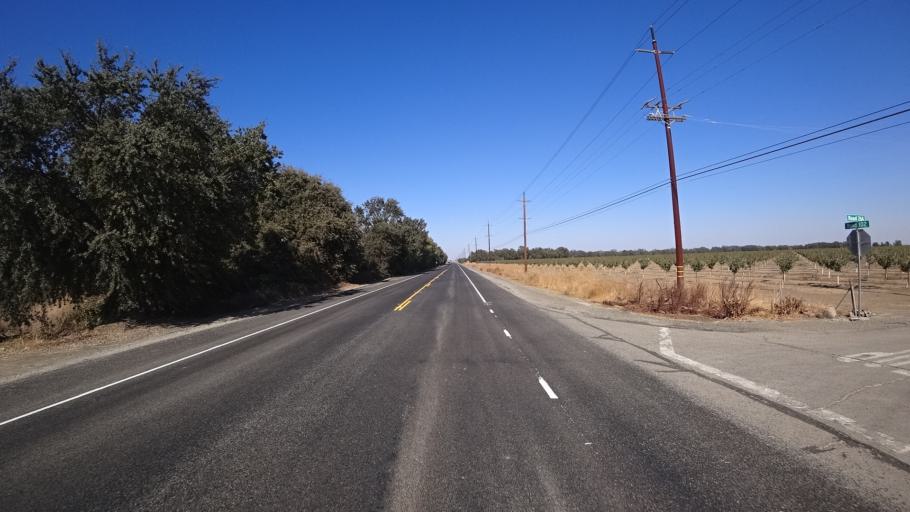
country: US
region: California
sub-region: Yolo County
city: Woodland
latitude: 38.6261
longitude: -121.7297
